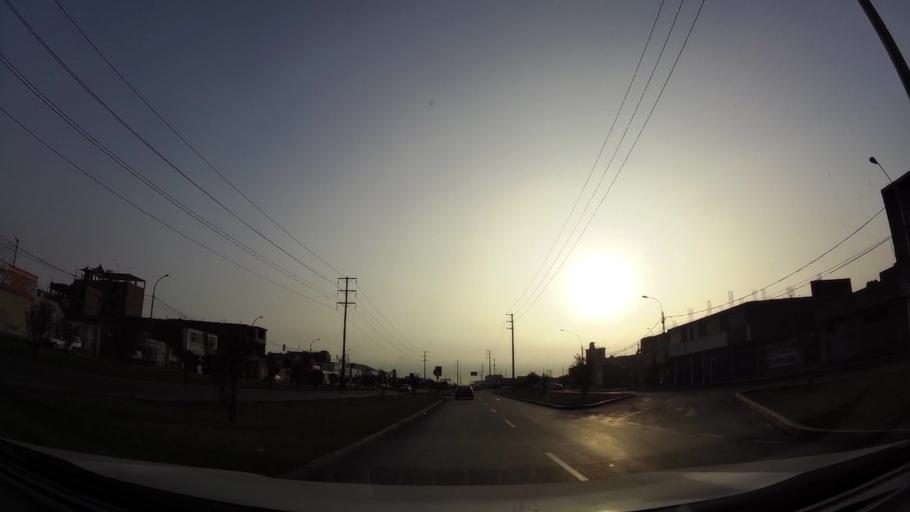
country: PE
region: Lima
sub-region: Lima
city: Independencia
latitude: -11.9894
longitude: -77.1026
